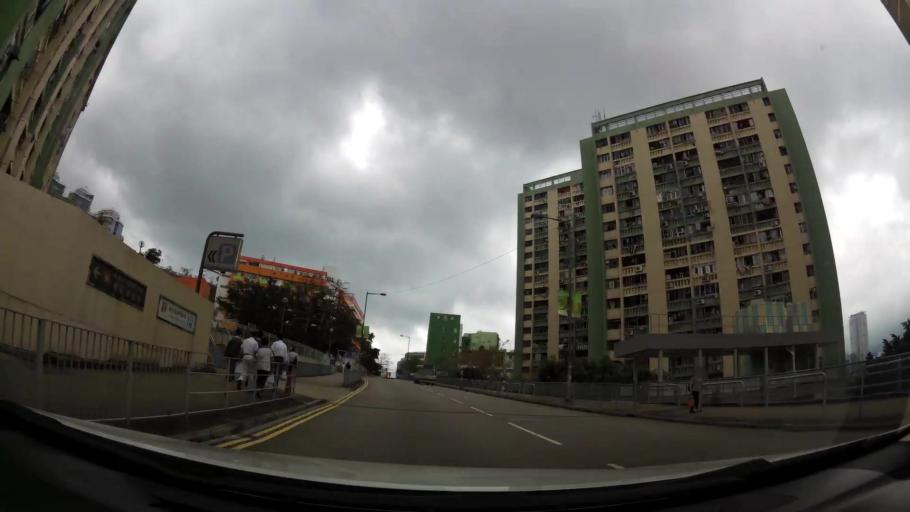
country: HK
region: Kowloon City
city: Kowloon
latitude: 22.3112
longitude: 114.1790
